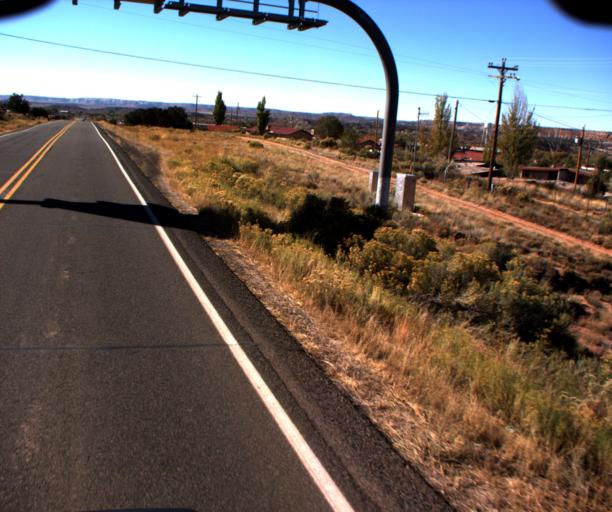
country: US
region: Arizona
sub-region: Apache County
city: Ganado
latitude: 35.7097
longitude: -109.5309
